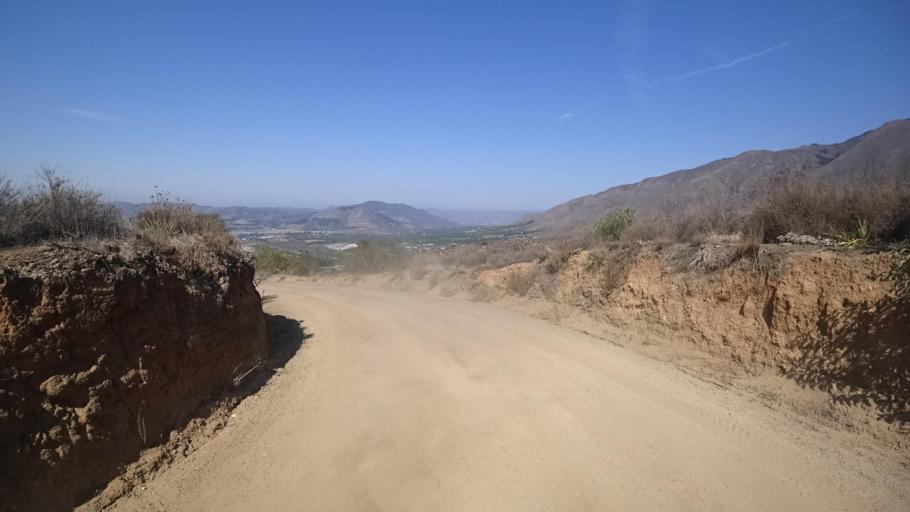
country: US
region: California
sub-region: San Diego County
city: Valley Center
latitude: 33.3272
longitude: -116.9656
